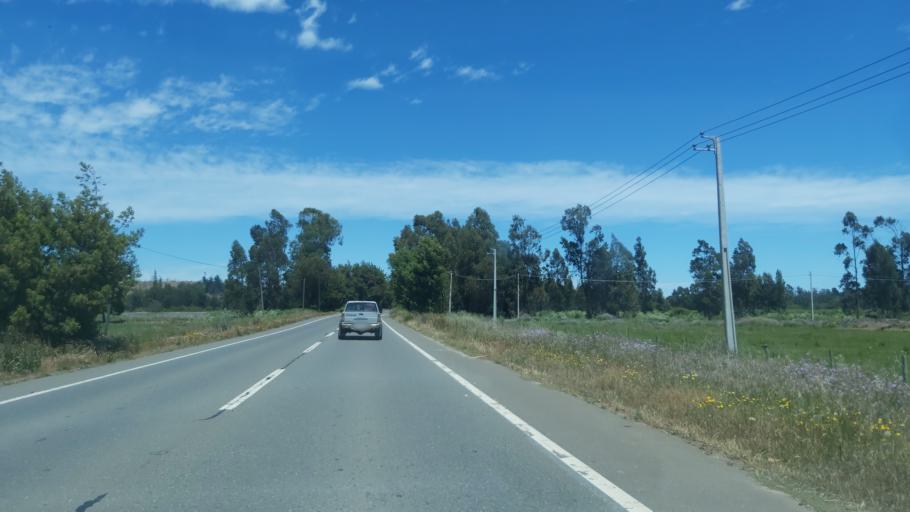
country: CL
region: Maule
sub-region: Provincia de Talca
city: Constitucion
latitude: -35.2974
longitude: -72.3708
